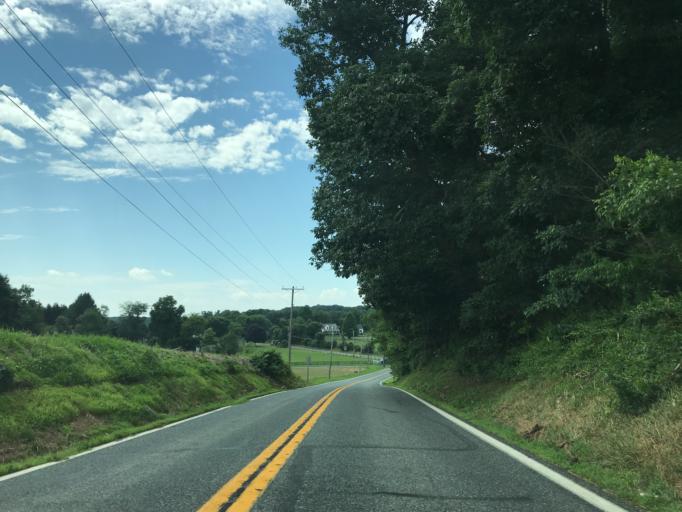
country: US
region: Pennsylvania
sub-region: York County
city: Susquehanna Trails
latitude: 39.6963
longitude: -76.4153
